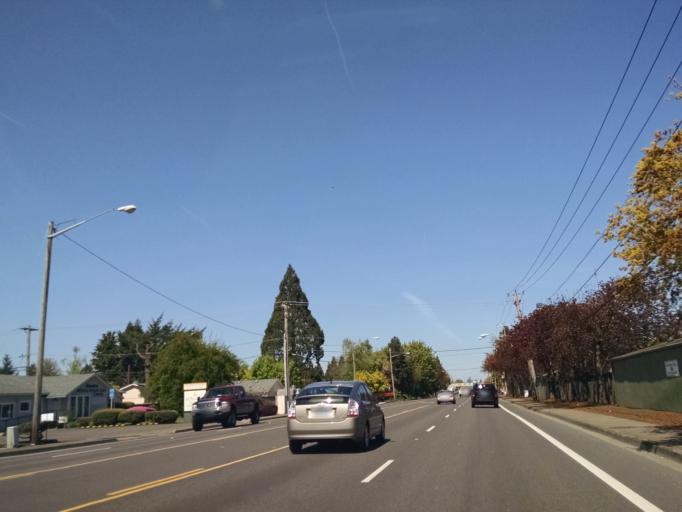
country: US
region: Oregon
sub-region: Lane County
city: Eugene
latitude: 44.0823
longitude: -123.0674
